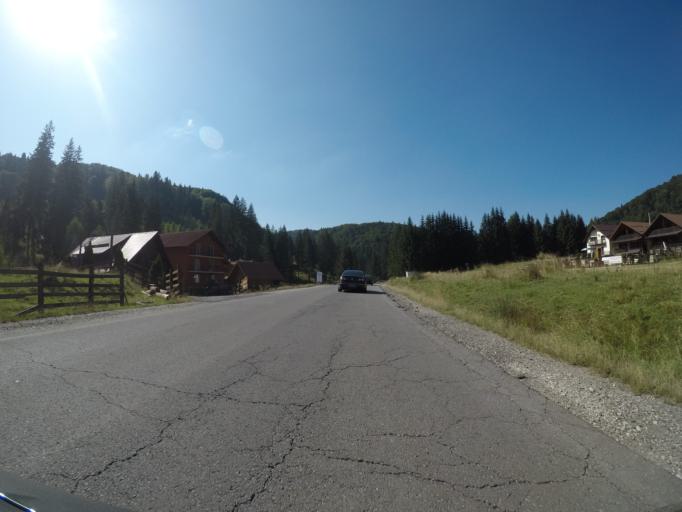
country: RO
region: Brasov
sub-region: Comuna Cristian
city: Cristian
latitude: 45.5912
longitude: 25.5264
